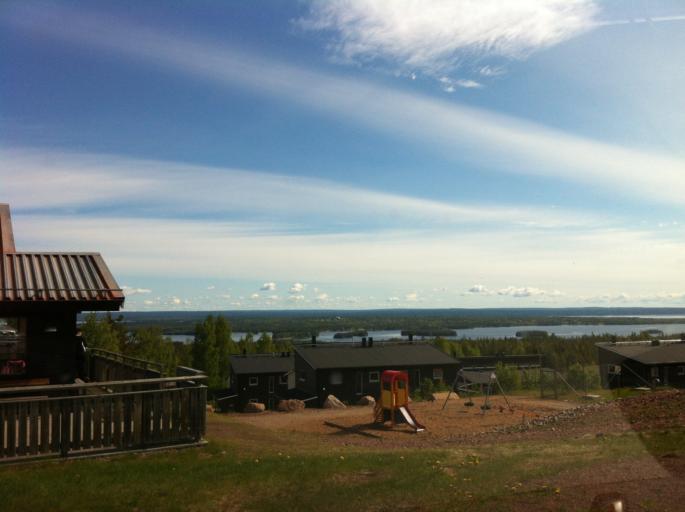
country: SE
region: Dalarna
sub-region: Mora Kommun
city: Mora
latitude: 60.8766
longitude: 14.5210
